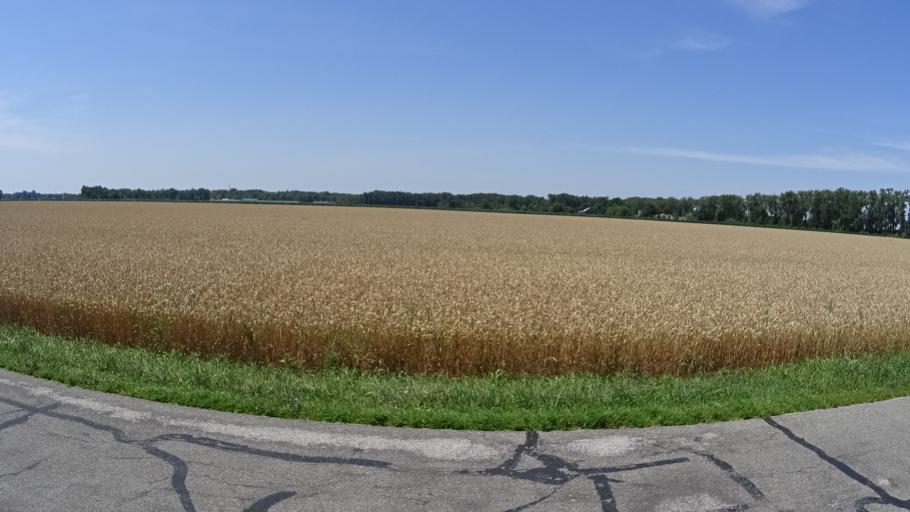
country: US
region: Ohio
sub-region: Erie County
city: Sandusky
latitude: 41.4207
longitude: -82.7909
